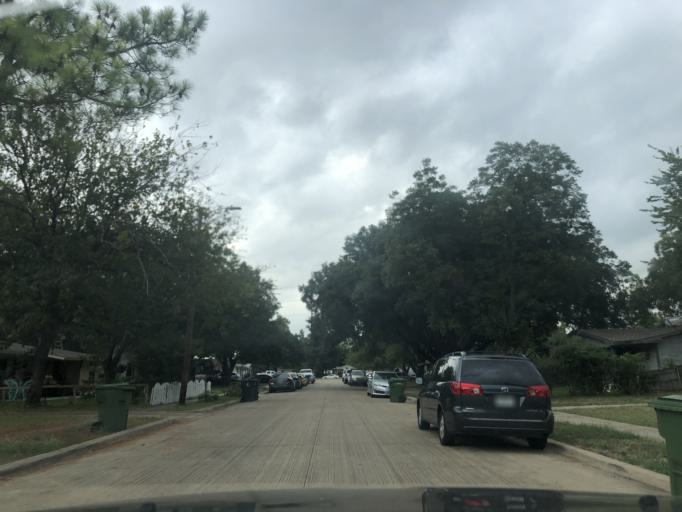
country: US
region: Texas
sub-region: Dallas County
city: Garland
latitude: 32.8887
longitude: -96.6498
